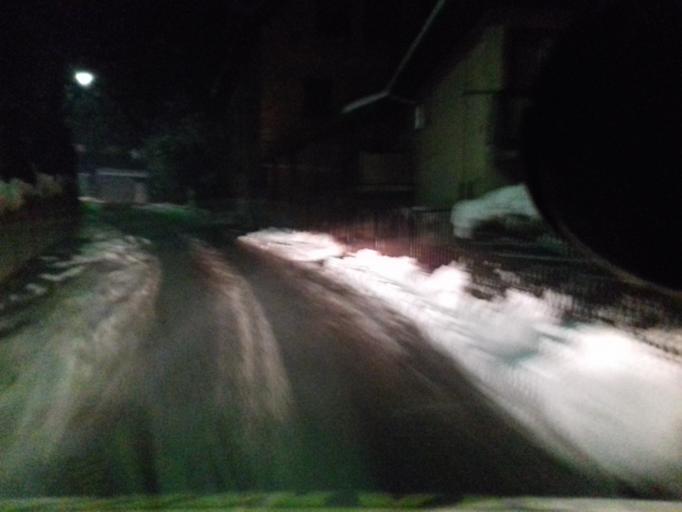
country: BA
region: Federation of Bosnia and Herzegovina
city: Kobilja Glava
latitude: 43.8724
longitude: 18.4334
